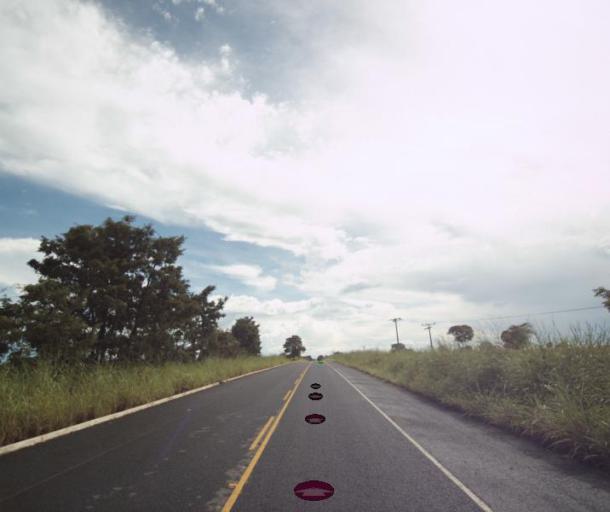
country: BR
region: Goias
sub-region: Sao Miguel Do Araguaia
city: Sao Miguel do Araguaia
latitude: -13.2939
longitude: -50.2274
